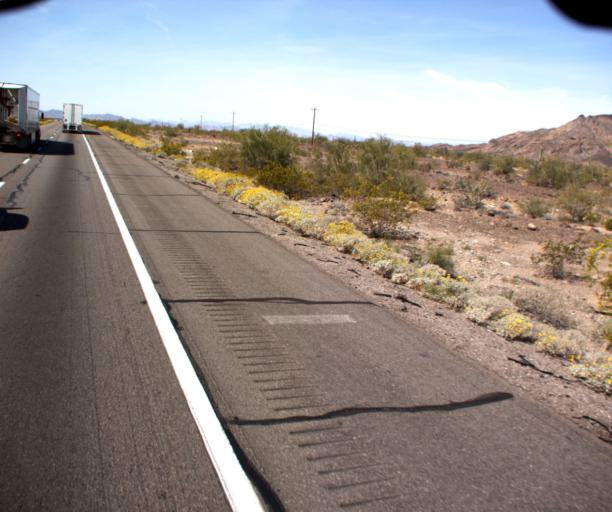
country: US
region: Arizona
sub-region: La Paz County
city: Quartzsite
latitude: 33.6790
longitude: -114.0739
